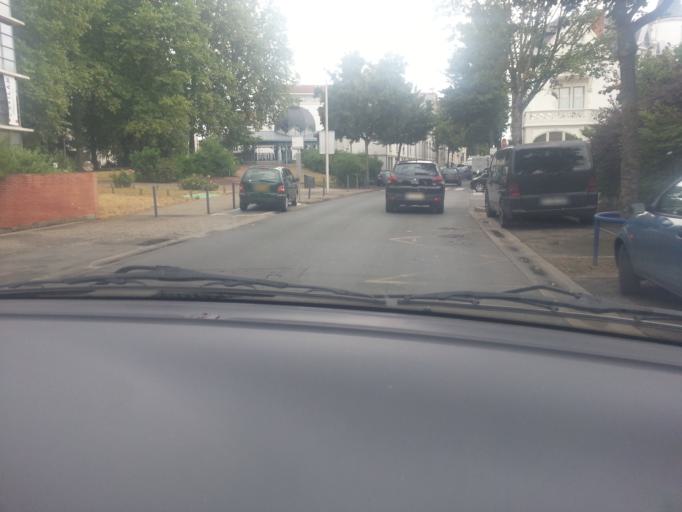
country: FR
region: Auvergne
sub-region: Departement de l'Allier
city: Vichy
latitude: 46.1195
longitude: 3.4256
